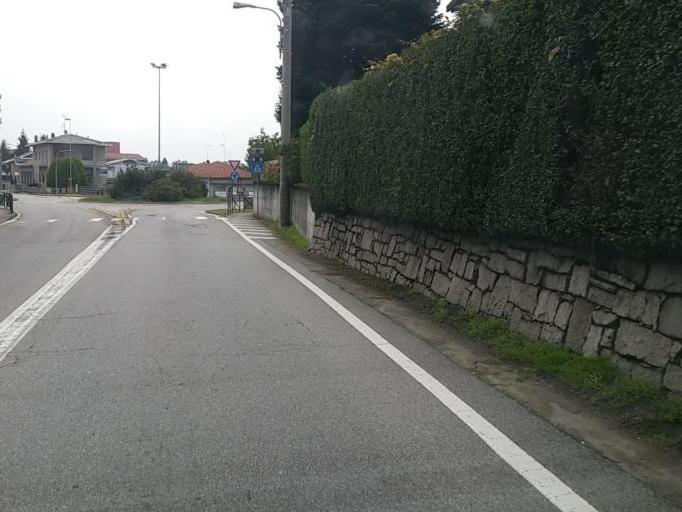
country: IT
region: Piedmont
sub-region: Provincia di Novara
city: Gozzano
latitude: 45.7458
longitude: 8.4301
